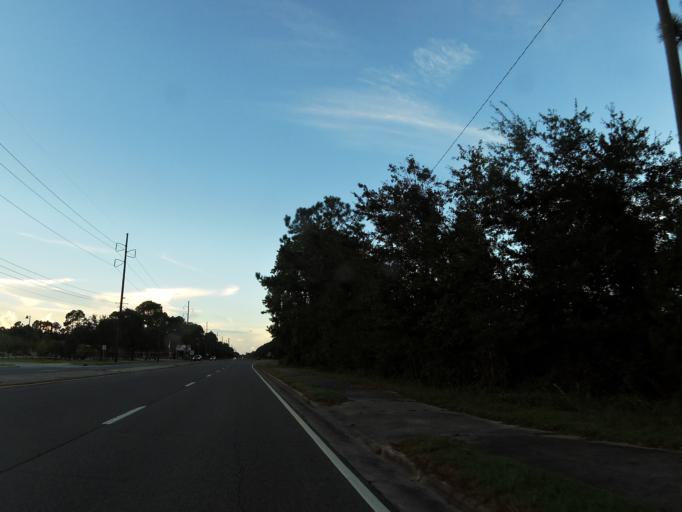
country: US
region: Georgia
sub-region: Camden County
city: St Marys
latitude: 30.7681
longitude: -81.5764
